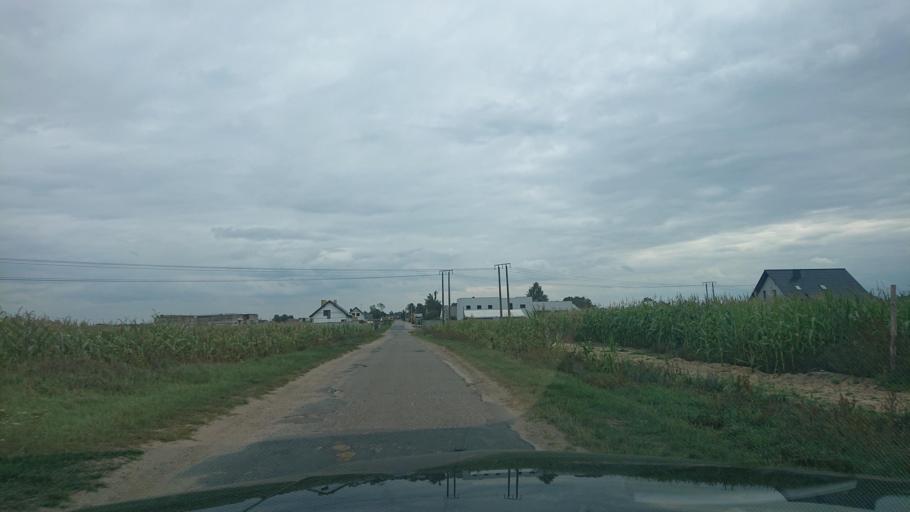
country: PL
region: Greater Poland Voivodeship
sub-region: Powiat gnieznienski
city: Niechanowo
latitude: 52.4765
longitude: 17.6199
